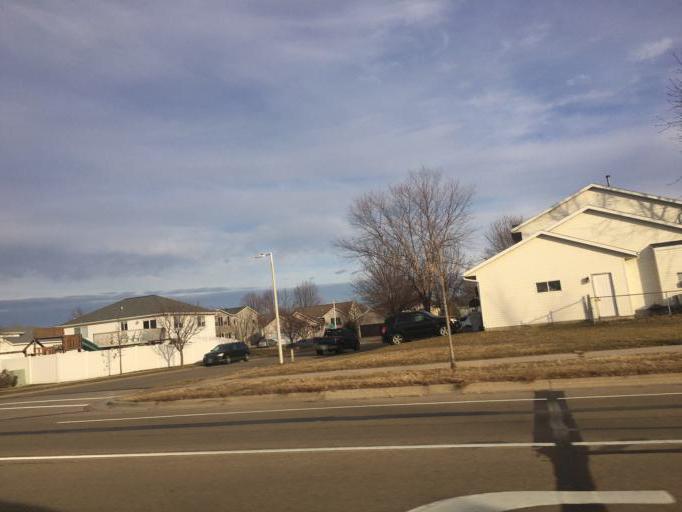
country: US
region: Minnesota
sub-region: Olmsted County
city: Oronoco
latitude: 44.0829
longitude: -92.5388
